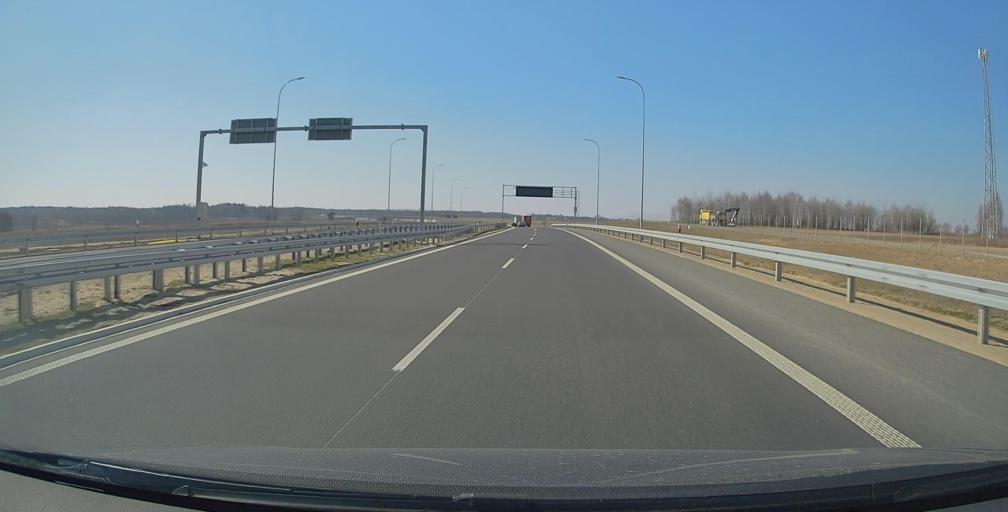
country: PL
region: Subcarpathian Voivodeship
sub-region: Powiat rzeszowski
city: Gorno
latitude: 50.3004
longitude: 22.1260
